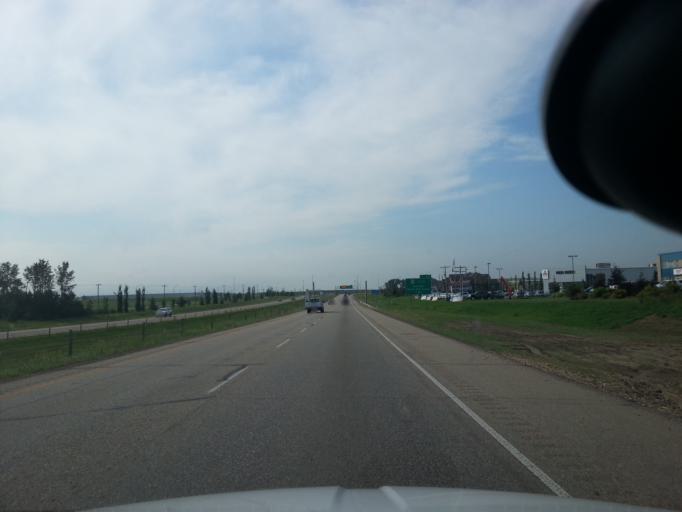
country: CA
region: Alberta
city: Red Deer
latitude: 52.2970
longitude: -113.8614
